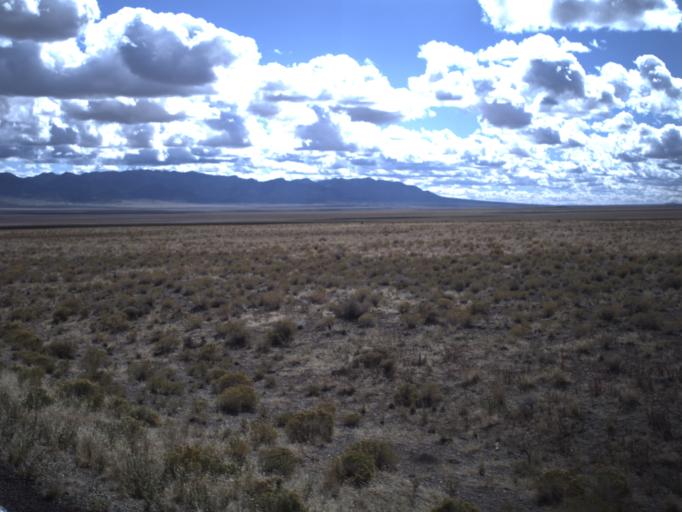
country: US
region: Utah
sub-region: Beaver County
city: Milford
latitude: 38.5725
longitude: -113.7907
